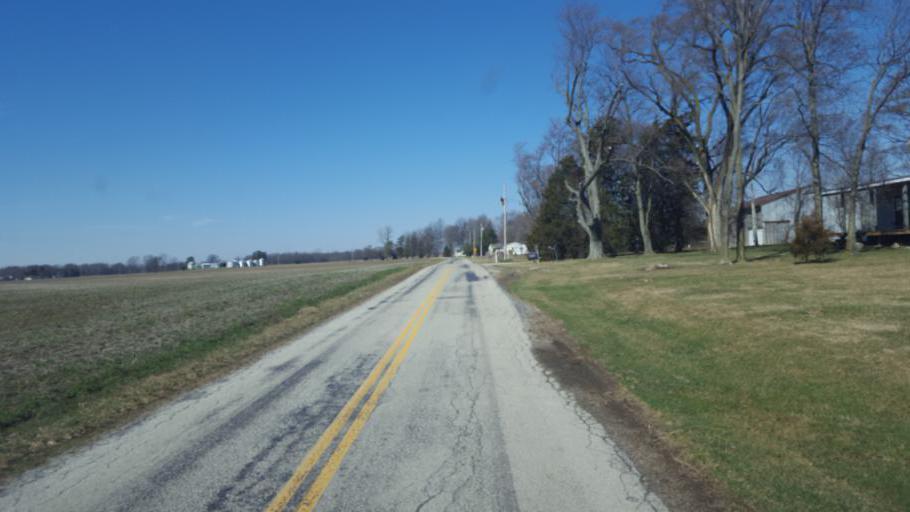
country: US
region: Ohio
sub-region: Morrow County
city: Cardington
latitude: 40.4900
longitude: -82.9754
